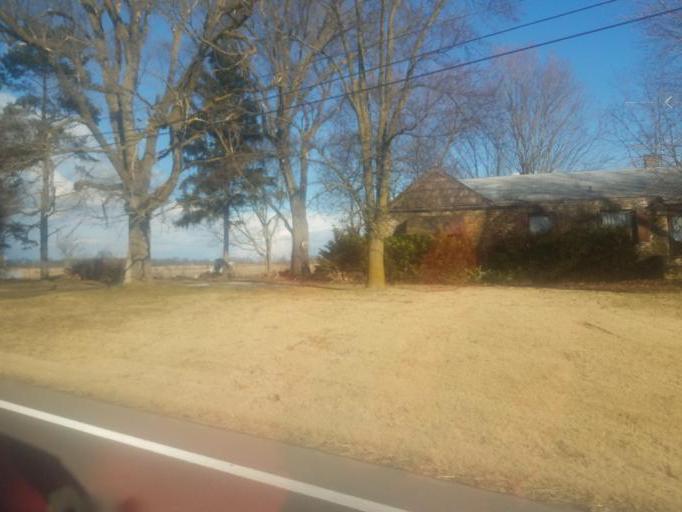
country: US
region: Ohio
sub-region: Marion County
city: Prospect
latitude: 40.3687
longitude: -83.1472
